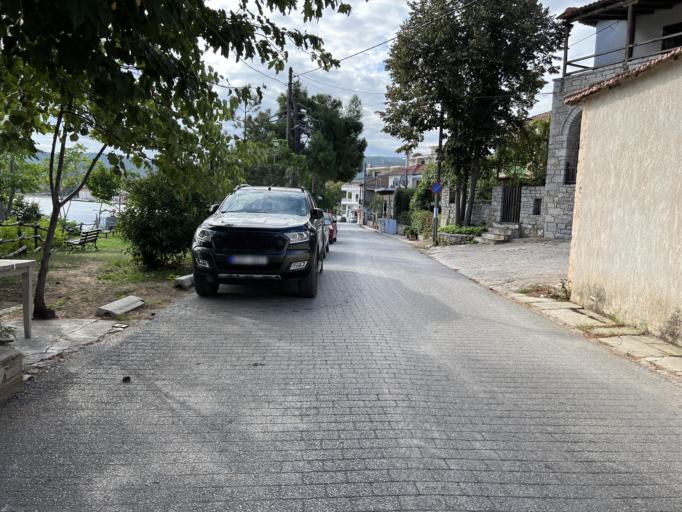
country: GR
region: Thessaly
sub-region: Nomos Magnisias
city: Sourpi
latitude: 39.1686
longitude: 22.8879
